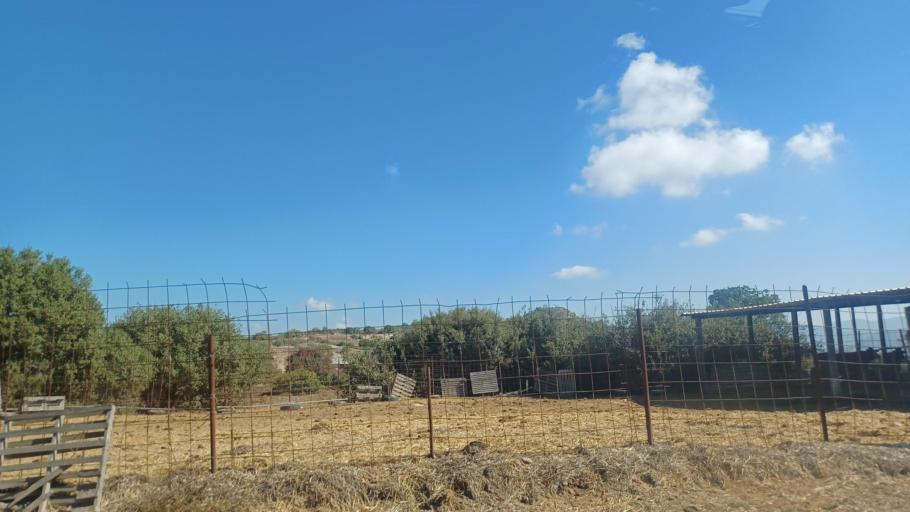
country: CY
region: Pafos
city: Polis
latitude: 34.9814
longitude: 32.5045
